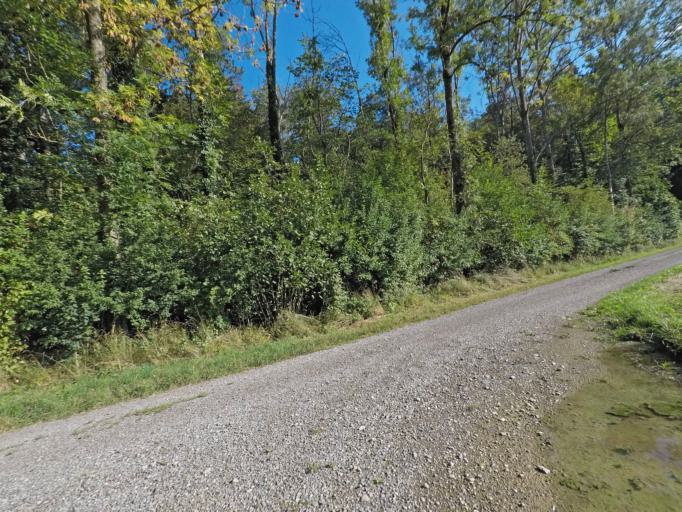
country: CH
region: Thurgau
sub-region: Frauenfeld District
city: Diessenhofen
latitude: 47.6566
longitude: 8.7416
